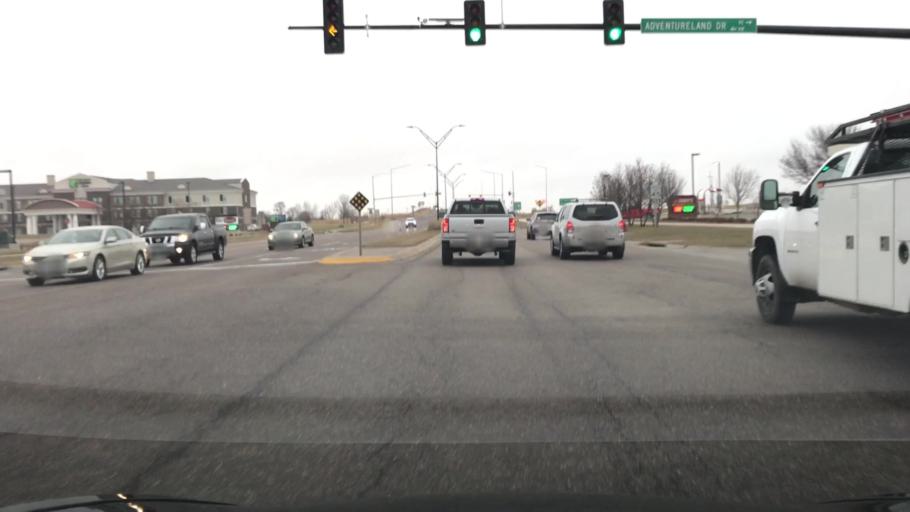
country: US
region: Iowa
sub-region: Polk County
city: Altoona
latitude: 41.6631
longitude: -93.4645
